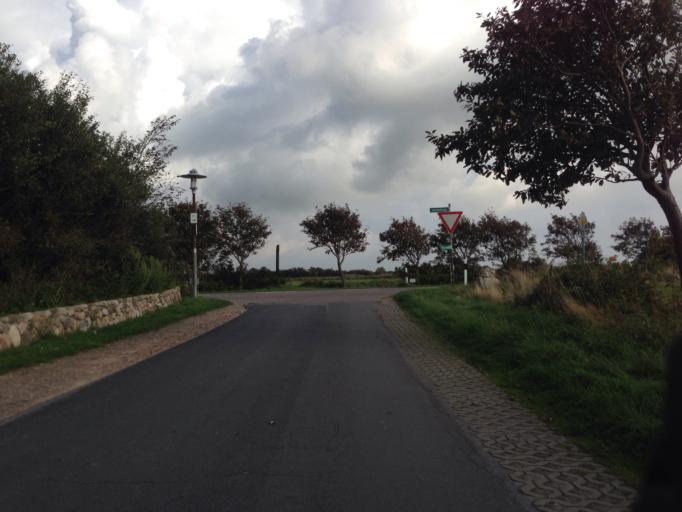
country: DE
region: Schleswig-Holstein
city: Utersum
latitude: 54.7078
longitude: 8.4052
